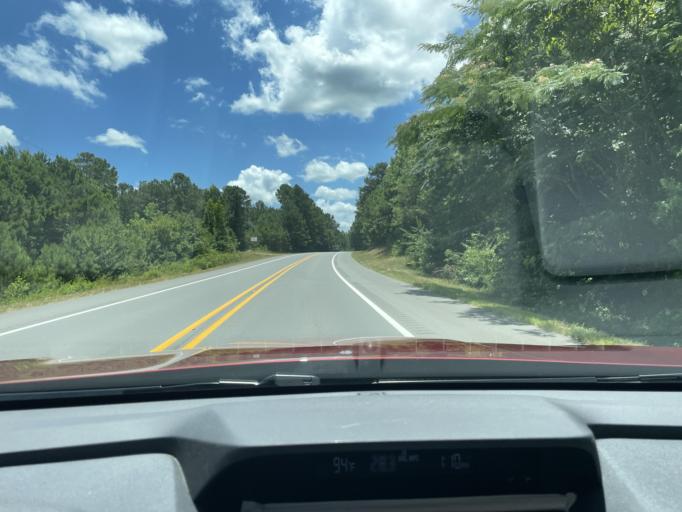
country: US
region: Arkansas
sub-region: Drew County
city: Monticello
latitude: 33.7236
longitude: -91.8108
